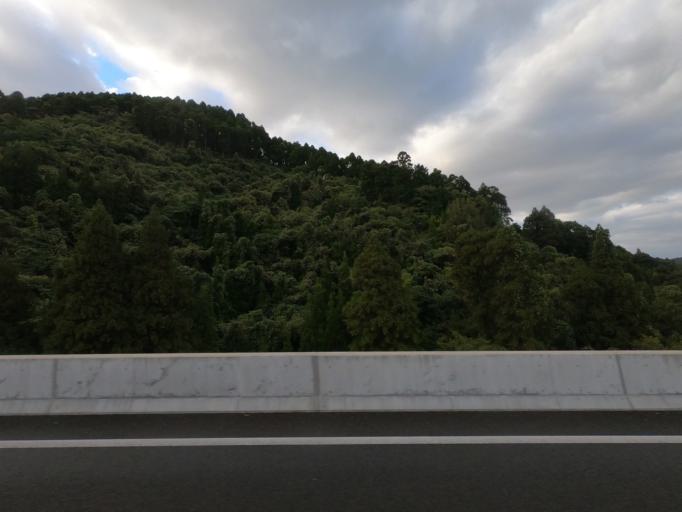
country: JP
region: Kumamoto
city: Minamata
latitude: 32.2242
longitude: 130.4325
